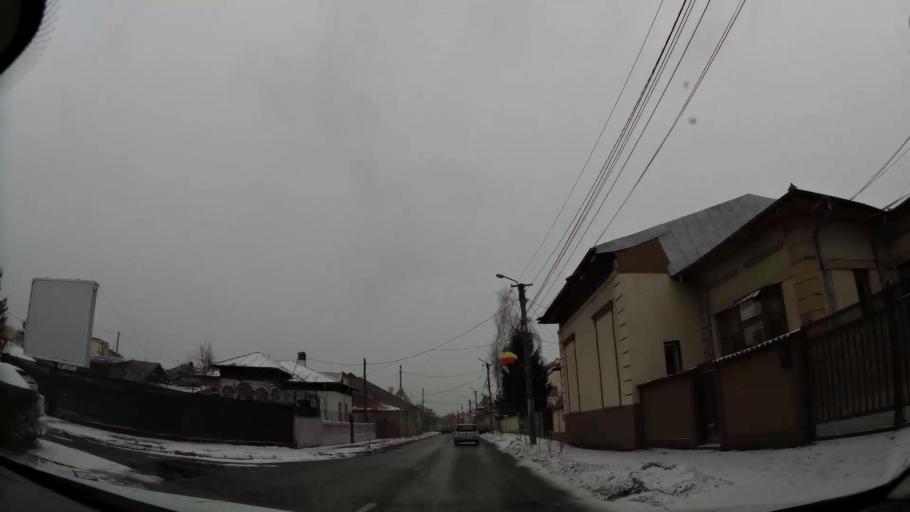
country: RO
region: Dambovita
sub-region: Municipiul Targoviste
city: Targoviste
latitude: 44.9275
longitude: 25.4491
